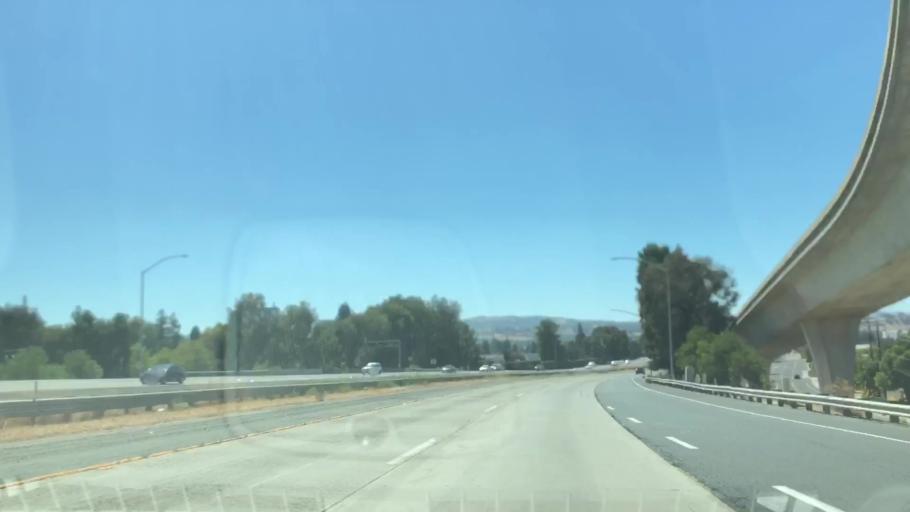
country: US
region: California
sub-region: Contra Costa County
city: Concord
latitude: 38.0051
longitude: -122.0382
